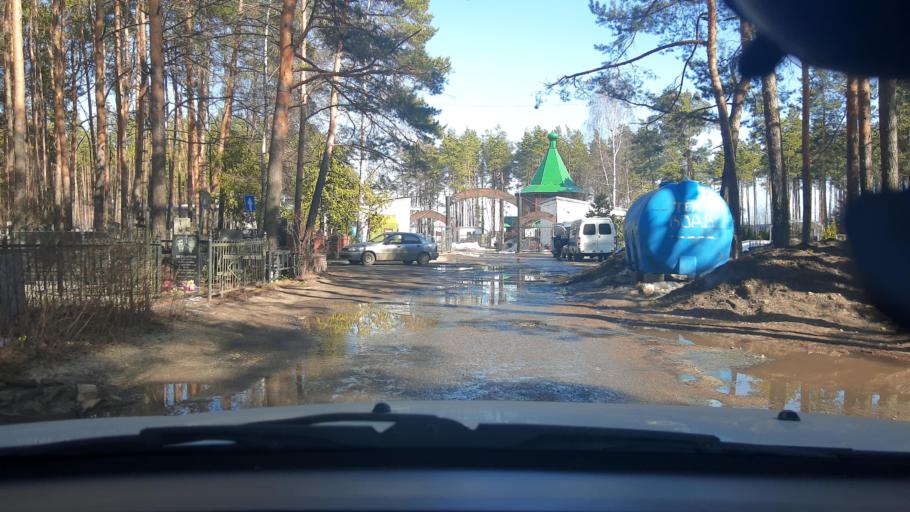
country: RU
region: Nizjnij Novgorod
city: Pyra
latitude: 56.2405
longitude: 43.3698
